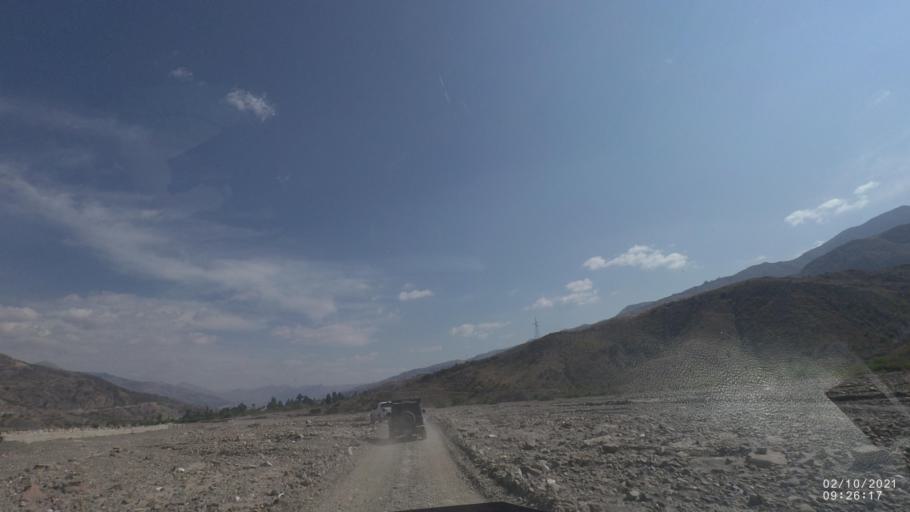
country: BO
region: Cochabamba
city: Irpa Irpa
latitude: -17.8592
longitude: -66.3130
